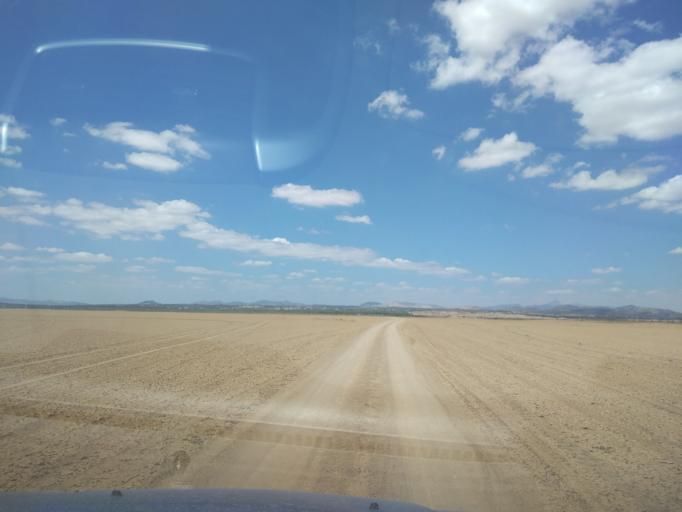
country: TN
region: Susah
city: Harqalah
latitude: 36.1617
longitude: 10.4585
